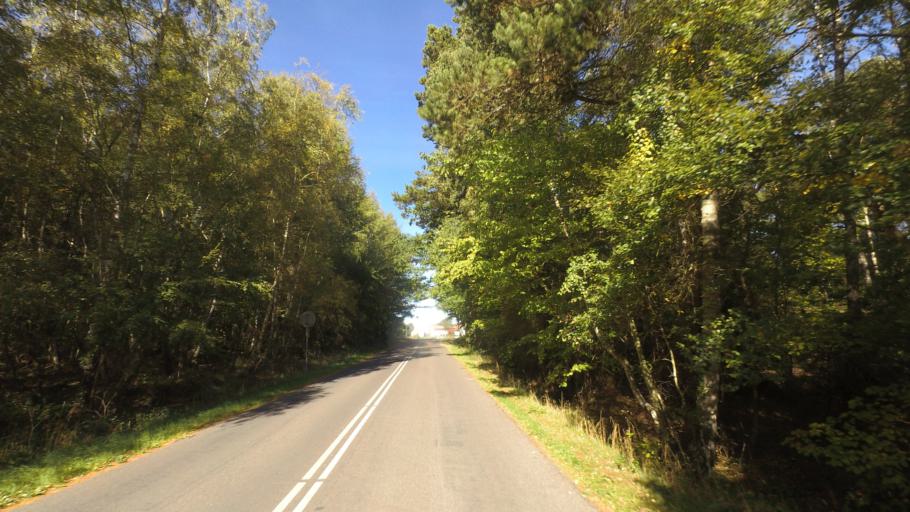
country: DK
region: Capital Region
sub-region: Bornholm Kommune
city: Nexo
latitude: 55.0007
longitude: 15.0752
